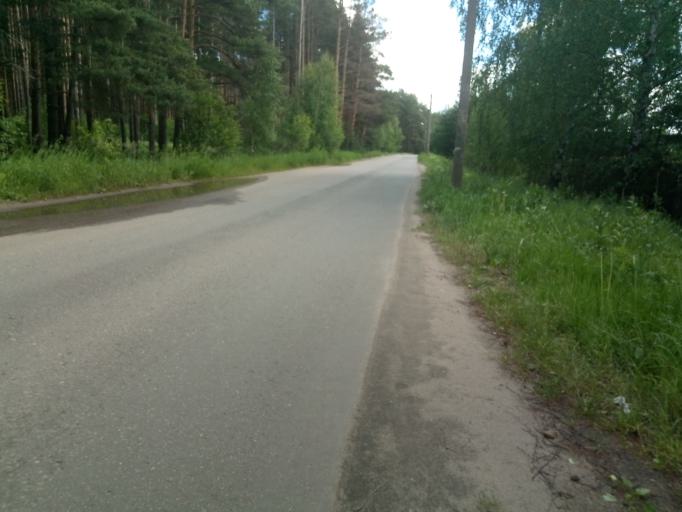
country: RU
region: Jaroslavl
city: Yaroslavl
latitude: 57.6570
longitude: 39.9760
